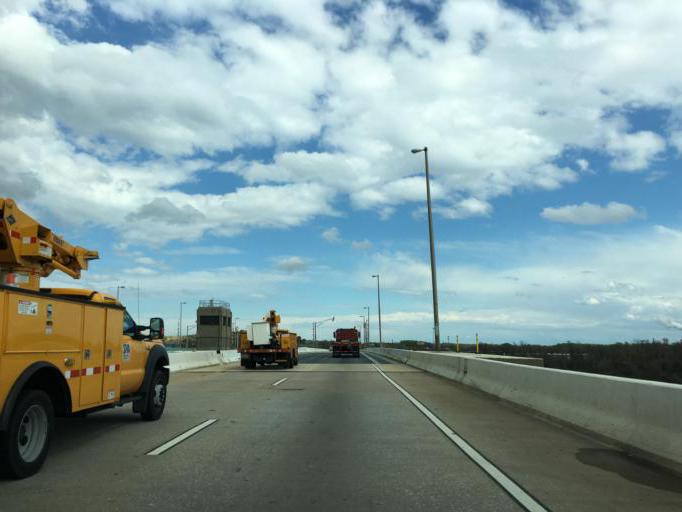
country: US
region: Maryland
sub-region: Anne Arundel County
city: Brooklyn Park
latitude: 39.2076
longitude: -76.5816
